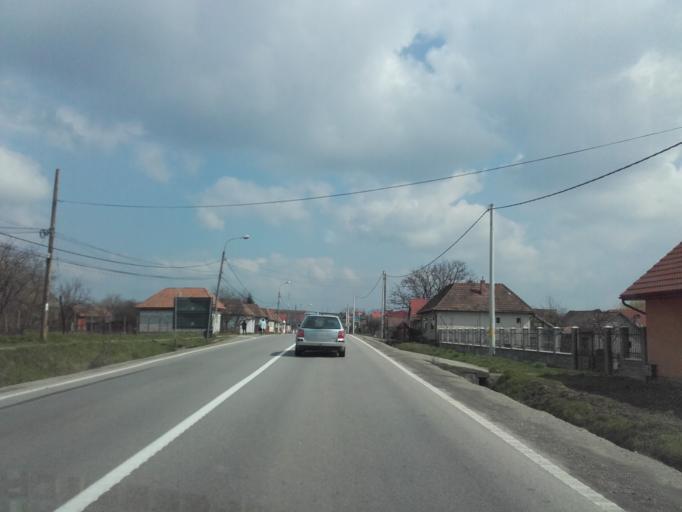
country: RO
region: Mures
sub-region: Comuna Sanpaul
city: Sanpaul
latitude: 46.4504
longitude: 24.3495
